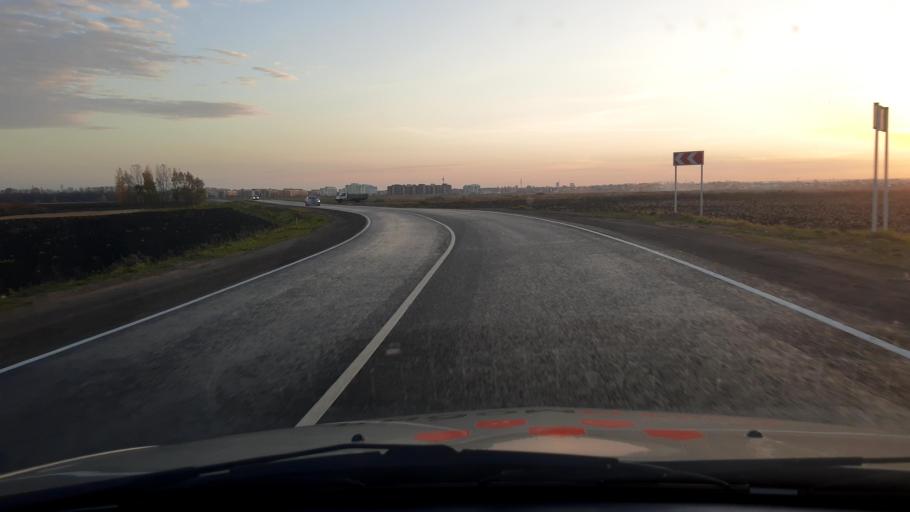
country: RU
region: Bashkortostan
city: Ufa
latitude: 54.8091
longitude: 55.9666
